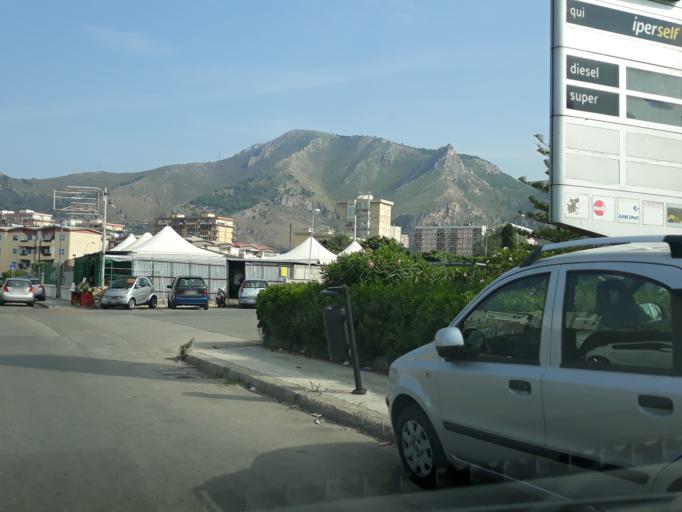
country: IT
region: Sicily
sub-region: Palermo
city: Villa Ciambra
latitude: 38.0851
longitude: 13.3541
